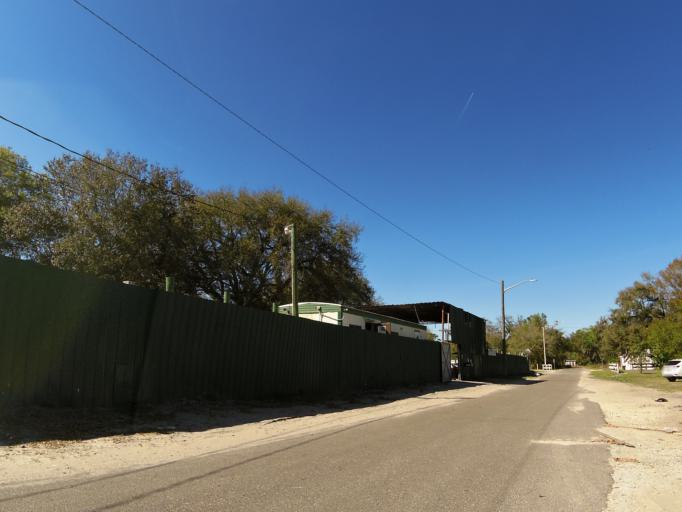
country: US
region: Florida
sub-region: Duval County
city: Jacksonville
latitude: 30.3589
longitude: -81.6475
